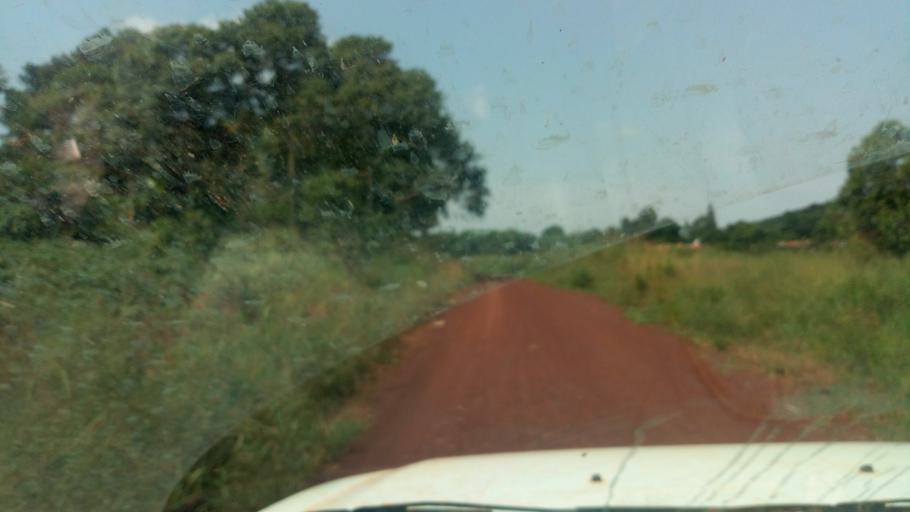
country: UG
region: Western Region
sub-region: Masindi District
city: Masindi
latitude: 1.6440
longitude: 31.8049
